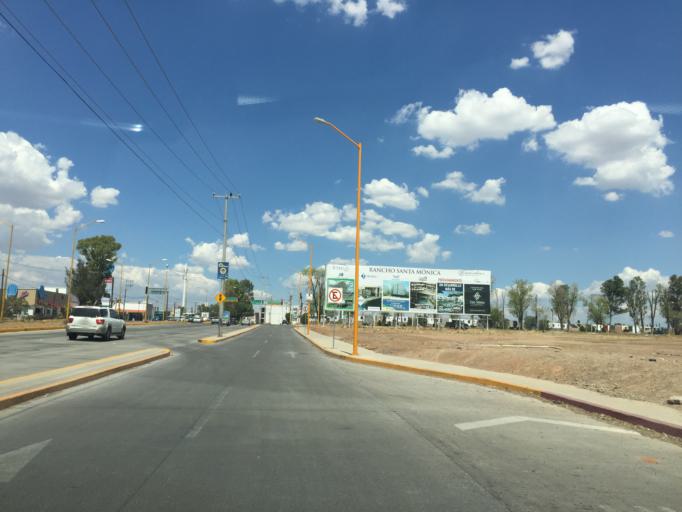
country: MX
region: Aguascalientes
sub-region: Aguascalientes
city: La Loma de los Negritos
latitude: 21.8429
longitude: -102.3219
